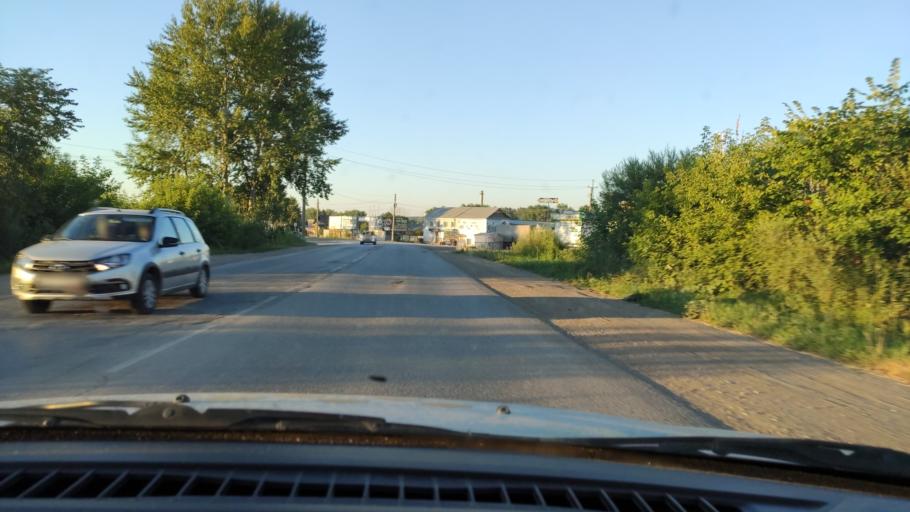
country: RU
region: Perm
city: Kungur
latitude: 57.4246
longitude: 56.9301
